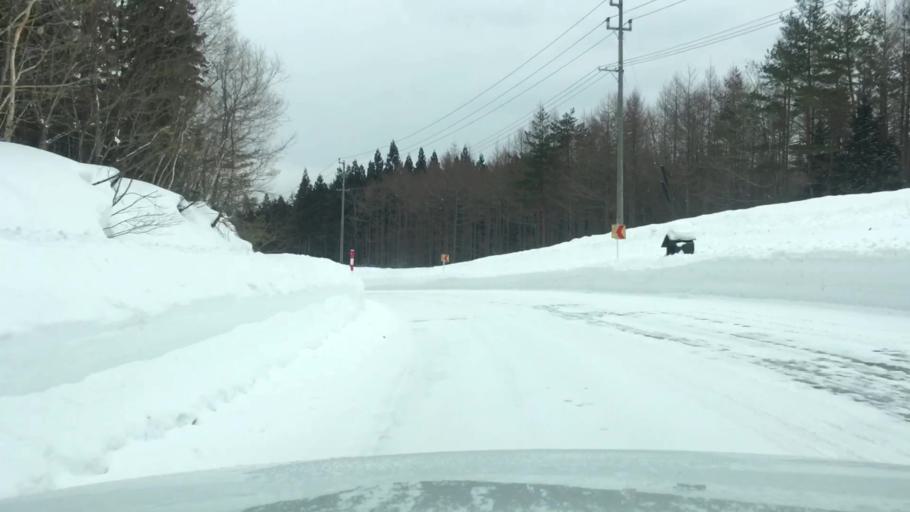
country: JP
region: Iwate
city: Shizukuishi
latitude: 39.9837
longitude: 141.0037
